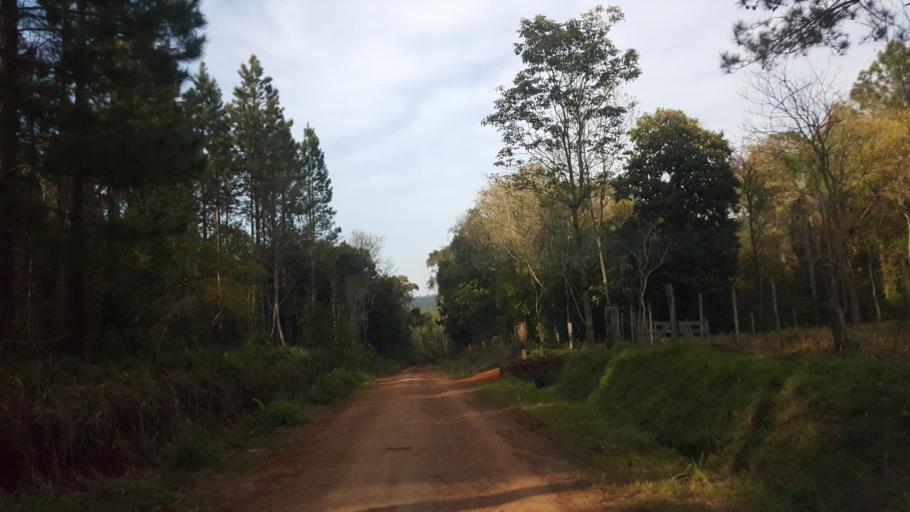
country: AR
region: Misiones
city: Capiovi
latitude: -26.8945
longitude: -55.1072
